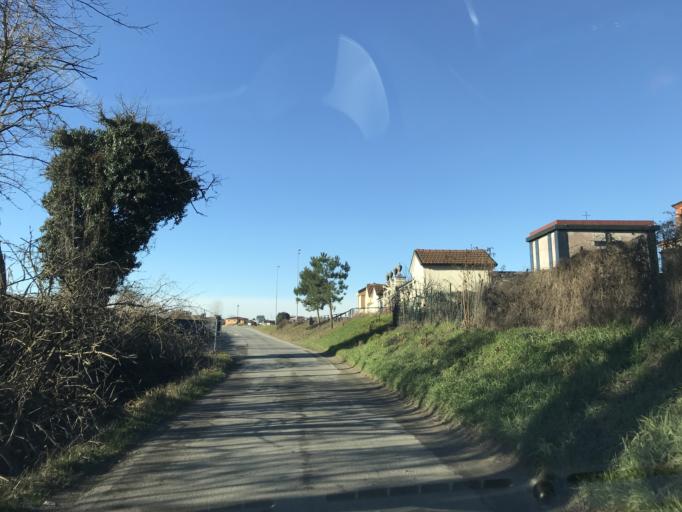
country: IT
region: Lombardy
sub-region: Provincia di Lodi
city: Bargano
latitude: 45.2356
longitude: 9.4508
